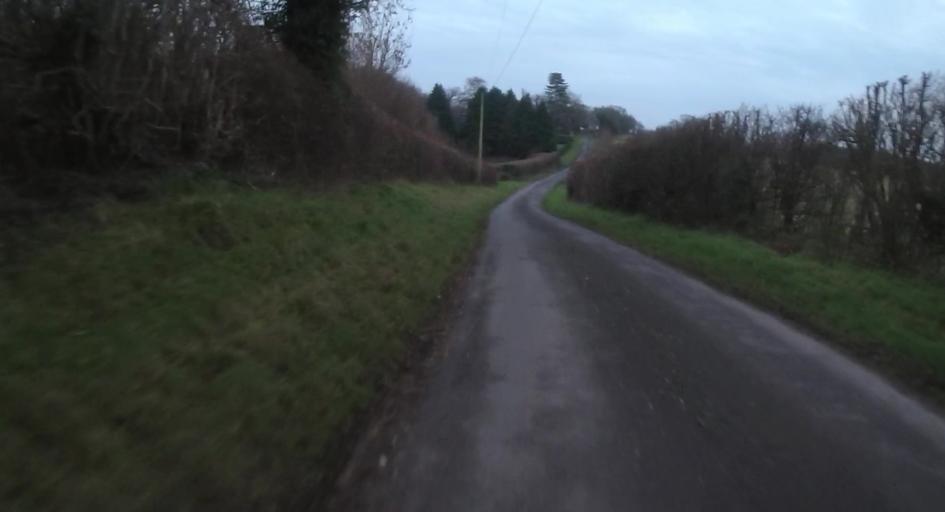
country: GB
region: England
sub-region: Hampshire
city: Overton
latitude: 51.2595
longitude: -1.3088
